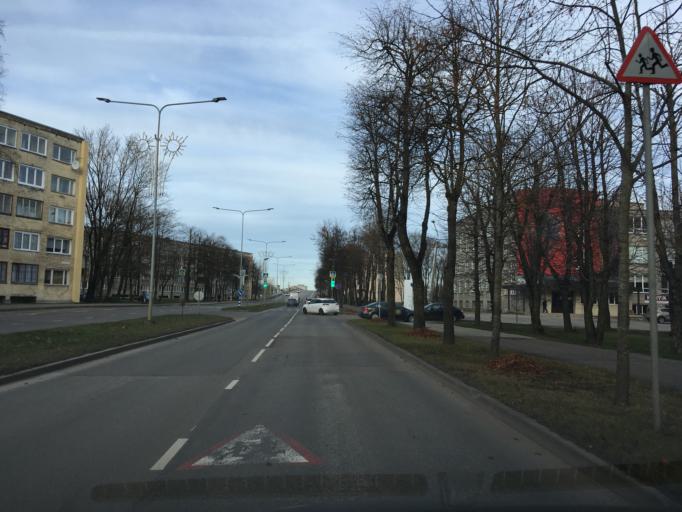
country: EE
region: Ida-Virumaa
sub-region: Narva linn
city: Narva
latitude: 59.3680
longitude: 28.1863
